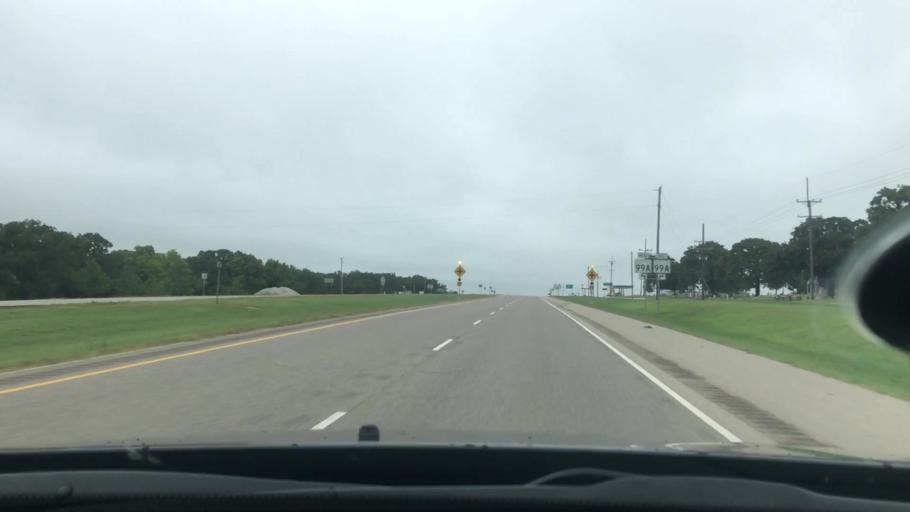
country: US
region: Oklahoma
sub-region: Seminole County
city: Seminole
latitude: 35.3453
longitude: -96.6715
